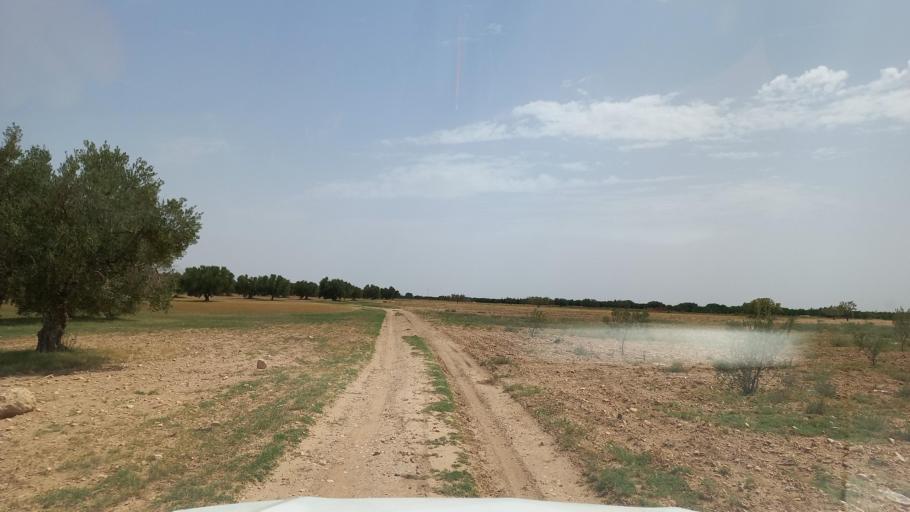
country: TN
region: Al Qasrayn
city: Kasserine
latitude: 35.2886
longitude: 9.0281
